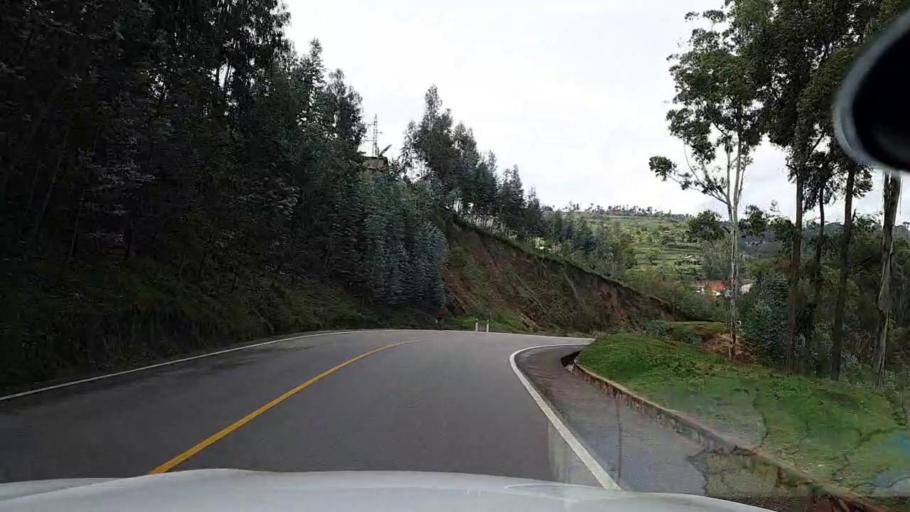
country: RW
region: Southern Province
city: Nzega
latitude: -2.5050
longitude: 29.5070
